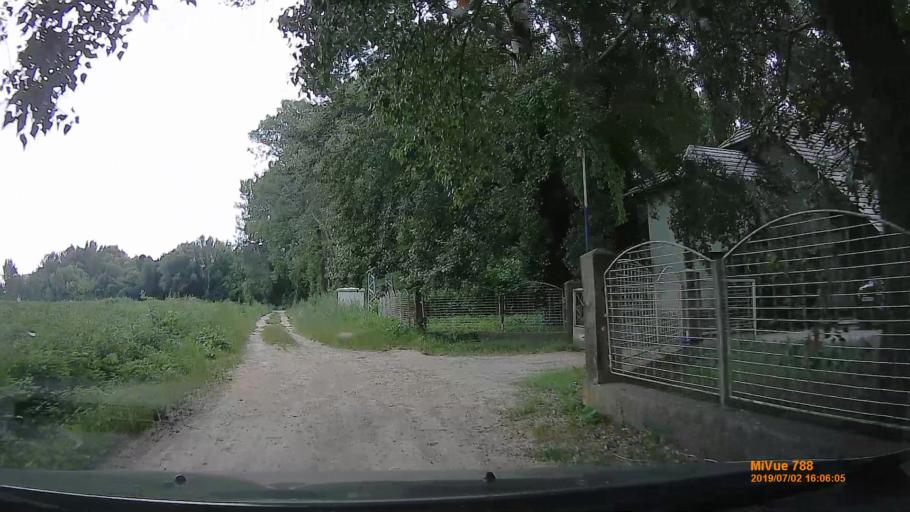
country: HU
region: Gyor-Moson-Sopron
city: Mosonmagyarovar
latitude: 47.8685
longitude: 17.2860
